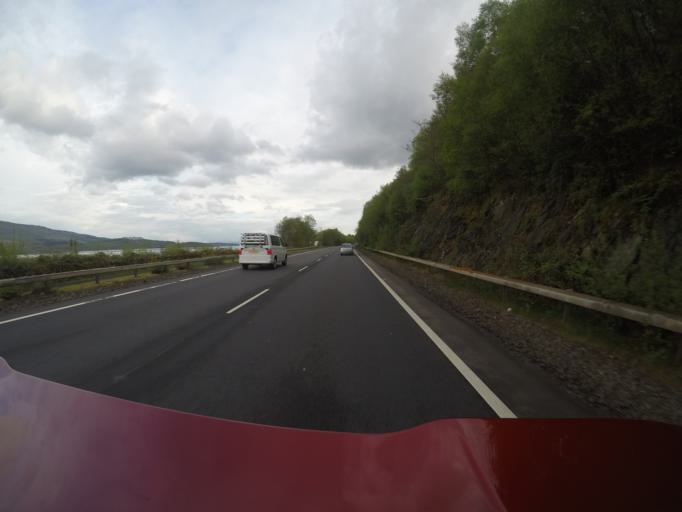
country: GB
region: Scotland
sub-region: Argyll and Bute
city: Helensburgh
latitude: 56.1404
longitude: -4.6614
